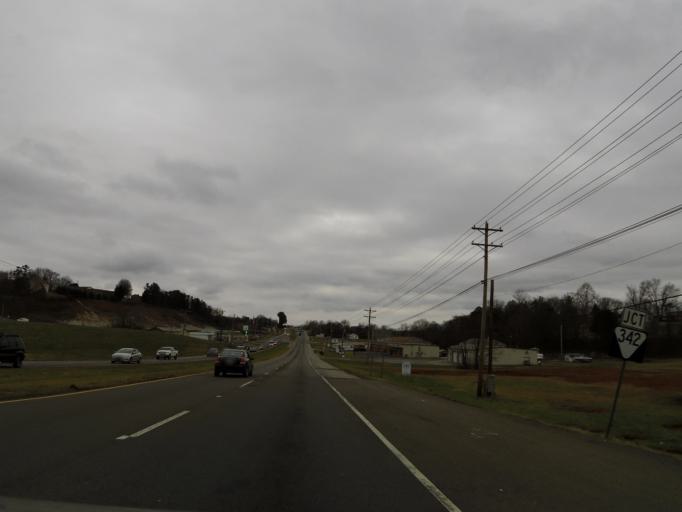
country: US
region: Tennessee
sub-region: Hamblen County
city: Morristown
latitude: 36.1837
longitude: -83.3774
